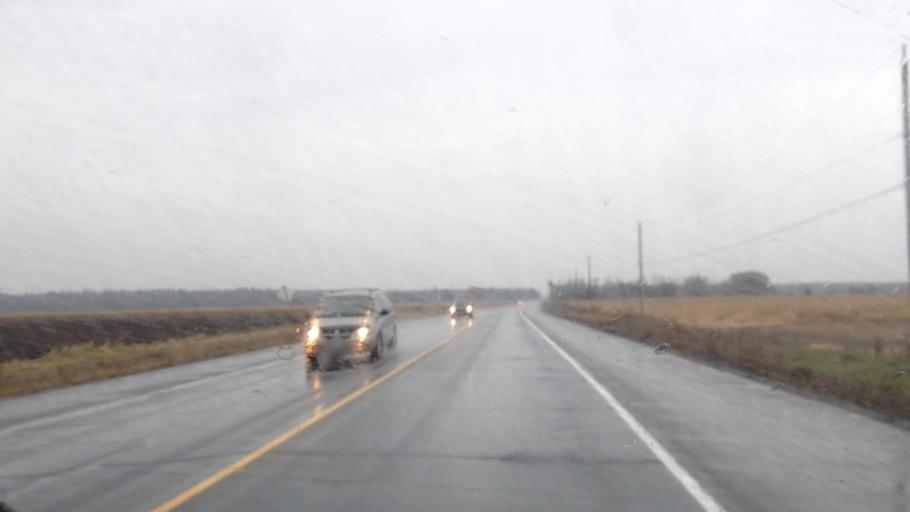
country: CA
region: Ontario
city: Clarence-Rockland
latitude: 45.4479
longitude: -75.4225
